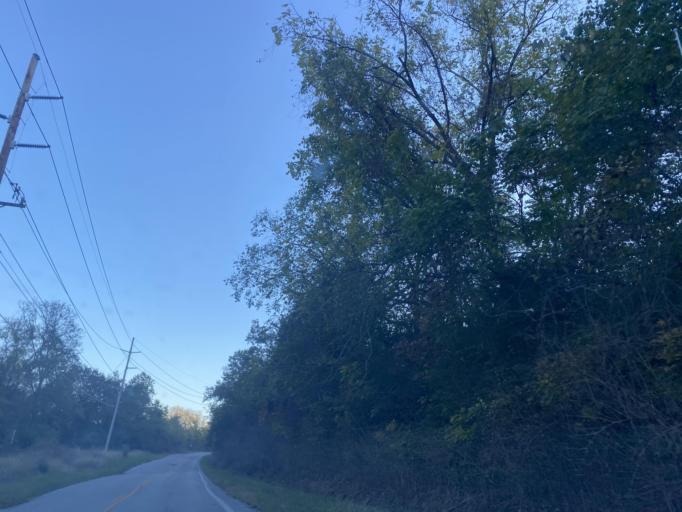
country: US
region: Kentucky
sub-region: Campbell County
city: Fort Thomas
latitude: 39.1014
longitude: -84.4410
